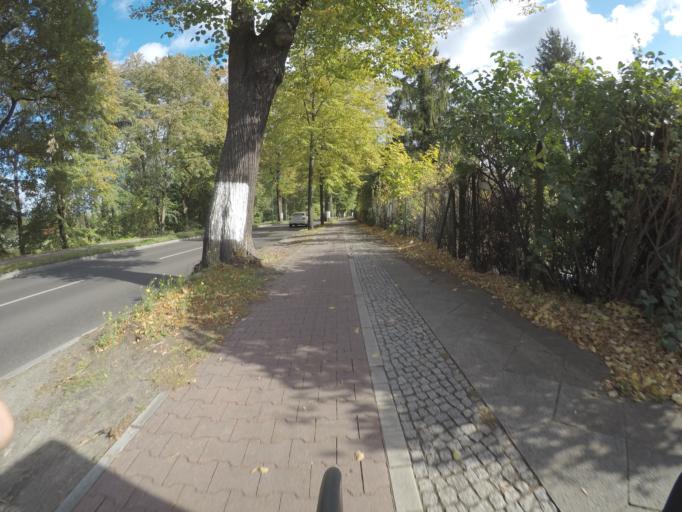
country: DE
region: Berlin
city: Siemensstadt
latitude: 52.5486
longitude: 13.2652
